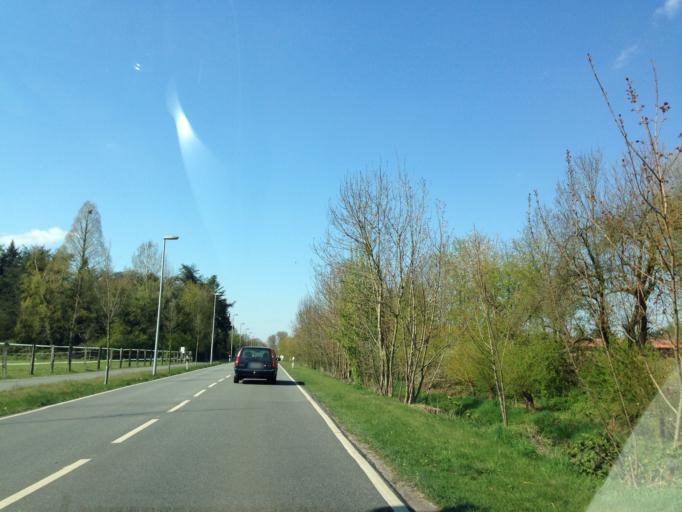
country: DE
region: North Rhine-Westphalia
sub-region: Regierungsbezirk Munster
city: Muenster
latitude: 51.9858
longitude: 7.6279
